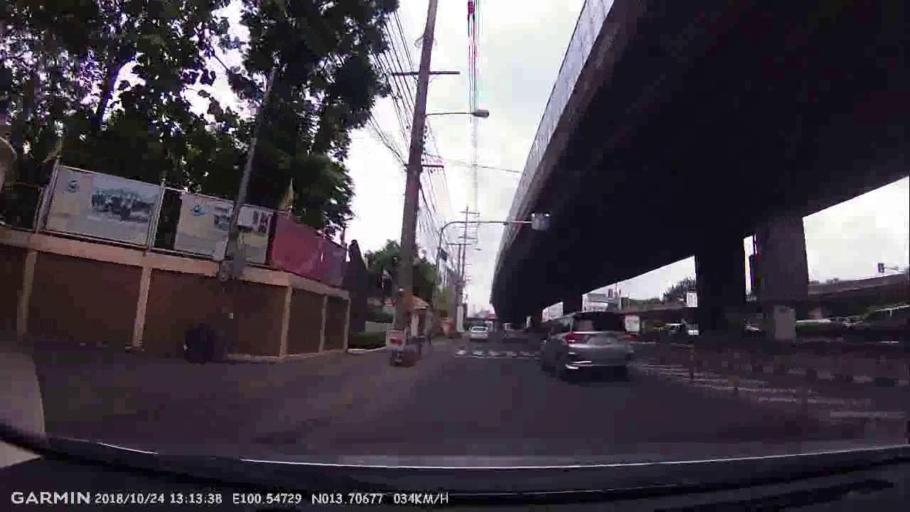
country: TH
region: Bangkok
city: Yan Nawa
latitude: 13.7068
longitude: 100.5473
